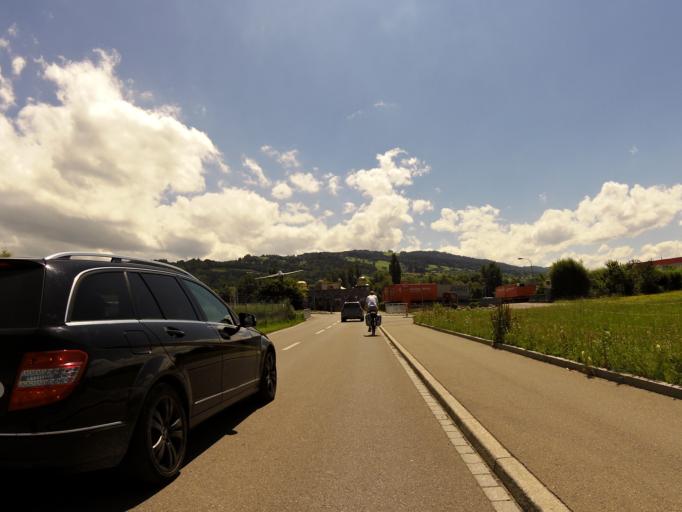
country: CH
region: Saint Gallen
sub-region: Wahlkreis Rheintal
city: Rheineck
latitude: 47.4864
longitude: 9.5492
